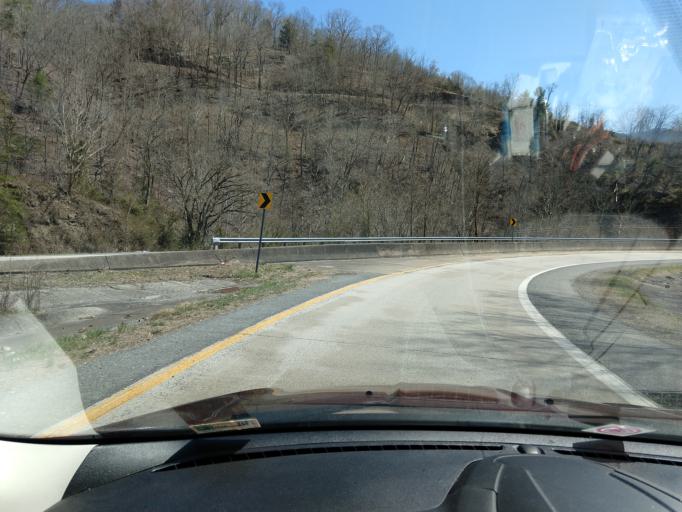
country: US
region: West Virginia
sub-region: Summers County
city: Hinton
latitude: 37.7810
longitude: -80.8919
